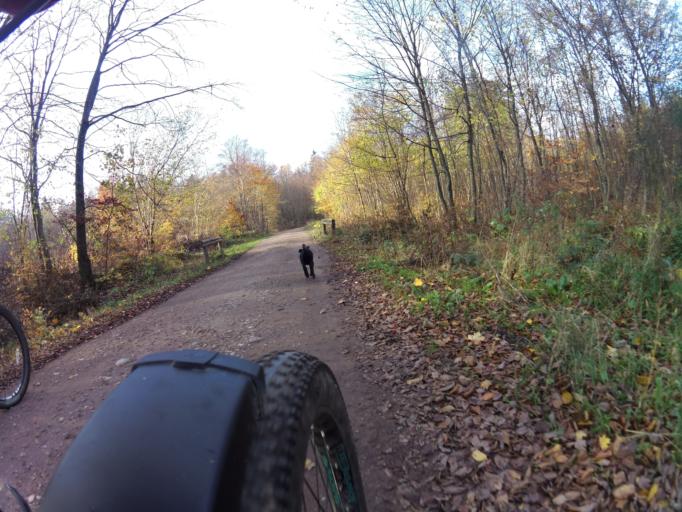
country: PL
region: Pomeranian Voivodeship
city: Strzelno
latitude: 54.7408
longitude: 18.2548
